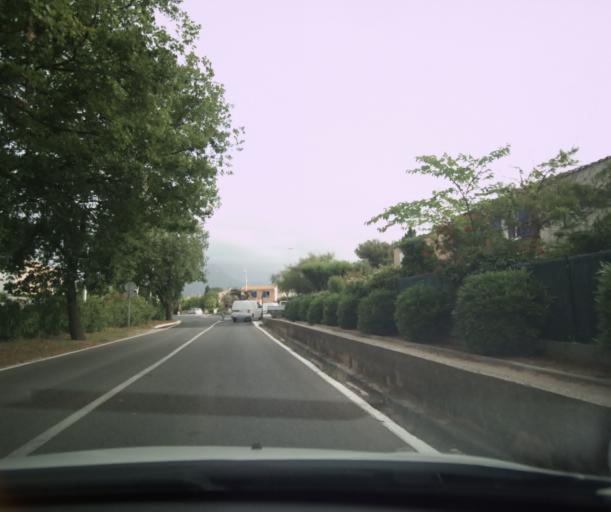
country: FR
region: Provence-Alpes-Cote d'Azur
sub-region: Departement du Var
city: Le Pradet
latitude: 43.1082
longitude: 6.0247
